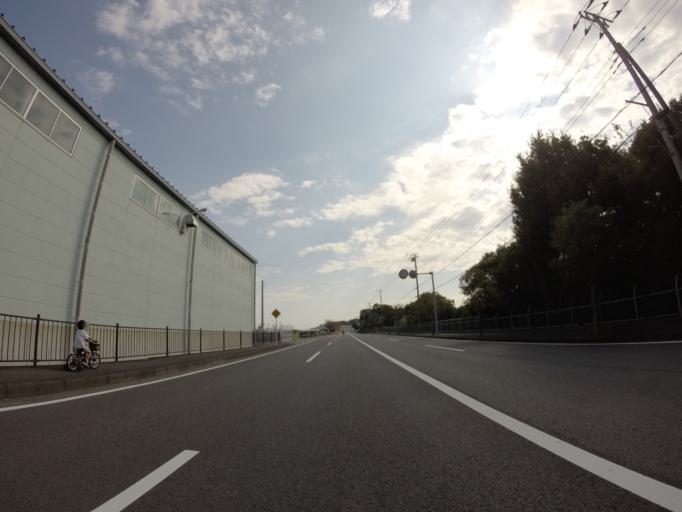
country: JP
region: Shizuoka
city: Fuji
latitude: 35.1410
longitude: 138.6885
